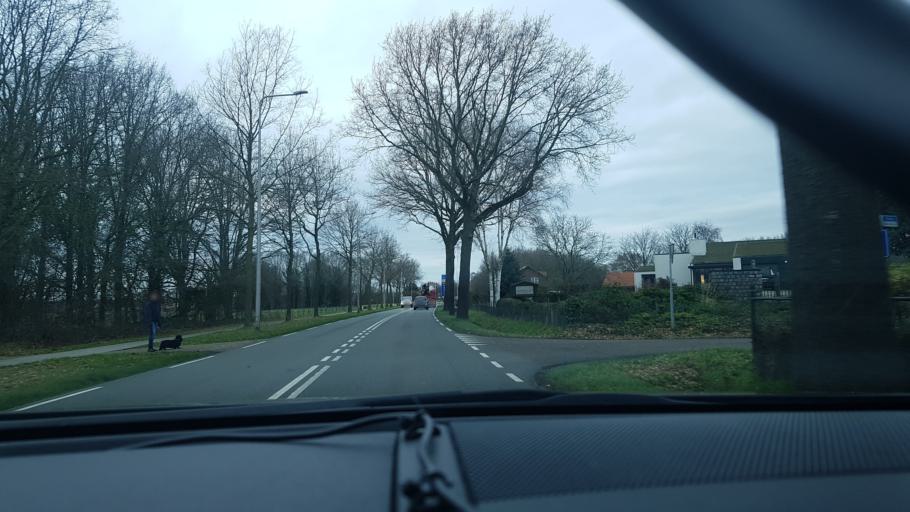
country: NL
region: Limburg
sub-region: Gemeente Leudal
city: Heythuysen
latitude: 51.2683
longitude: 5.9176
